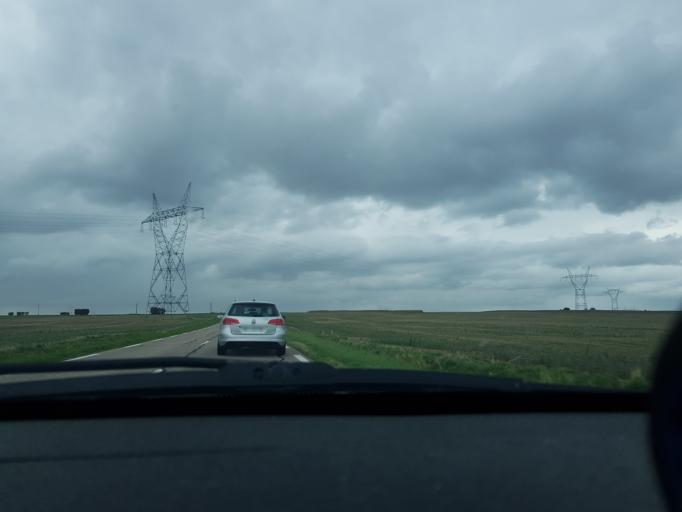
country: FR
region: Lorraine
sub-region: Departement de la Moselle
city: Faulquemont
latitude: 48.9926
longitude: 6.5990
